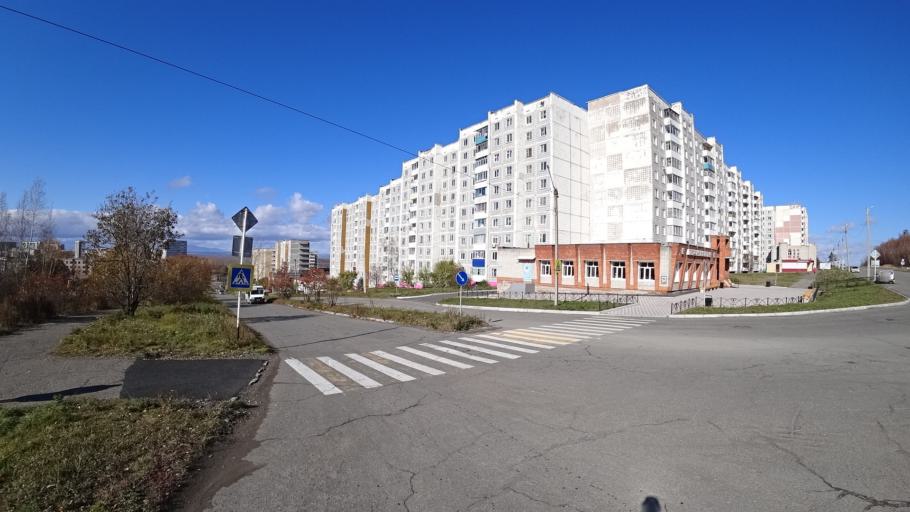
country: RU
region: Khabarovsk Krai
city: Amursk
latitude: 50.2425
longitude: 136.9200
